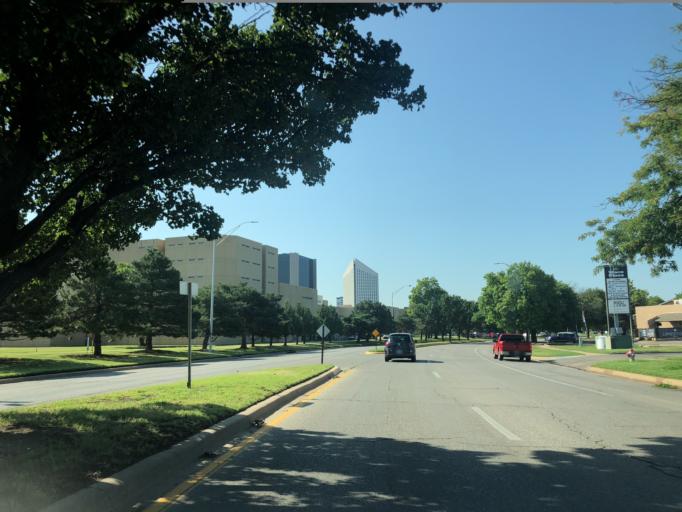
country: US
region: Kansas
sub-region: Sedgwick County
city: Wichita
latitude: 37.6967
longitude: -97.3413
